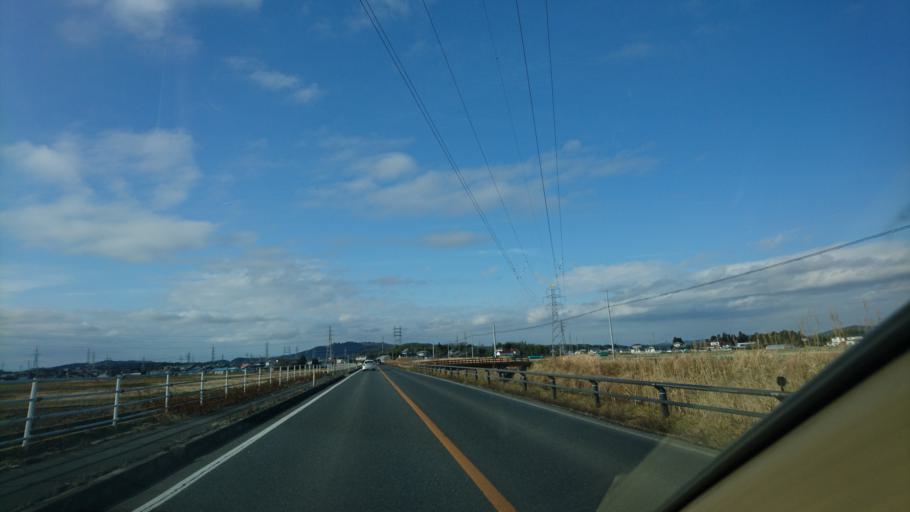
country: JP
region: Miyagi
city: Yamoto
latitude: 38.4708
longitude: 141.2312
